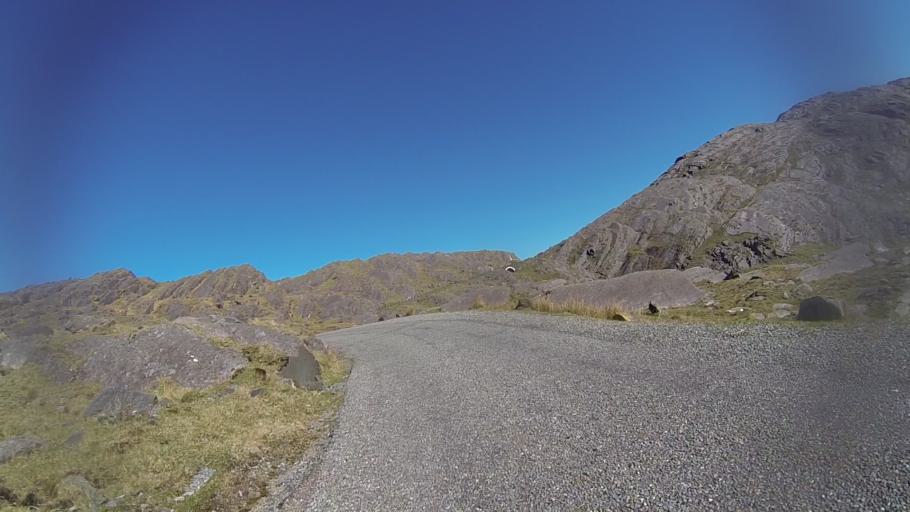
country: IE
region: Munster
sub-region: Ciarrai
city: Kenmare
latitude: 51.7185
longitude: -9.7551
